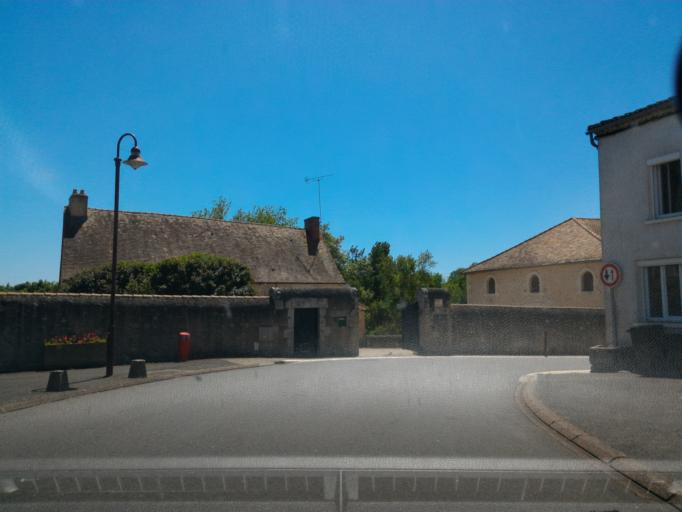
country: FR
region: Poitou-Charentes
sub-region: Departement de la Vienne
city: Terce
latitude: 46.4116
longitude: 0.5938
